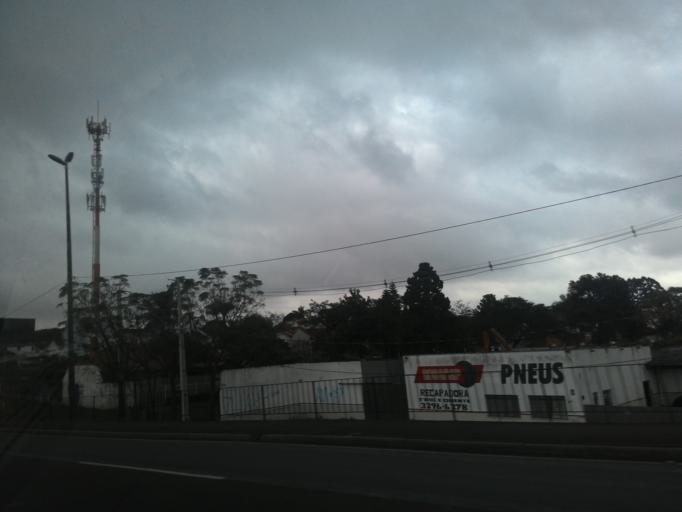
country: BR
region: Parana
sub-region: Curitiba
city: Curitiba
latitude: -25.4540
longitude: -49.2427
